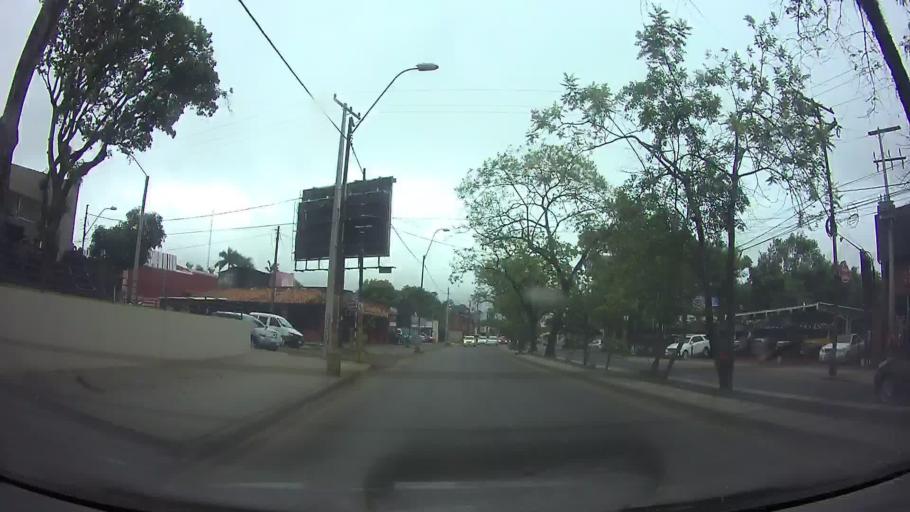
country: PY
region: Central
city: Fernando de la Mora
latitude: -25.3044
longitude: -57.5391
